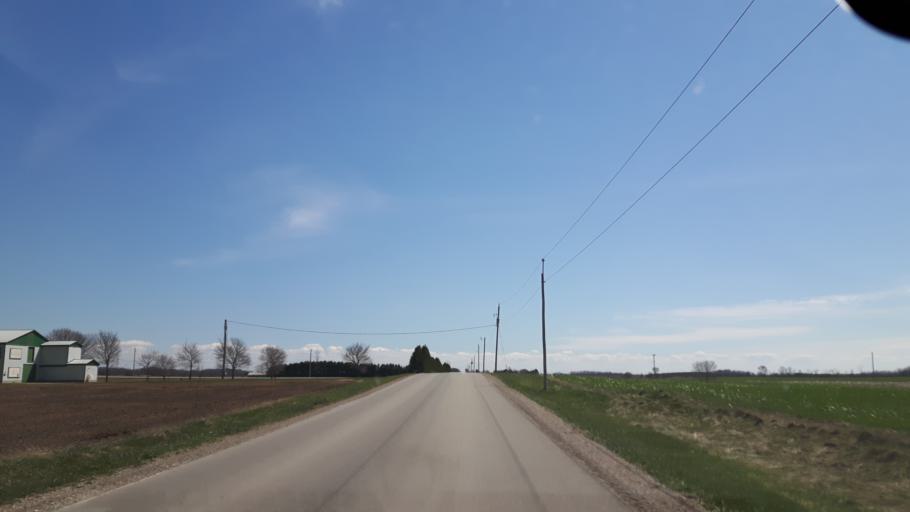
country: CA
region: Ontario
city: Goderich
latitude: 43.6447
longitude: -81.6440
